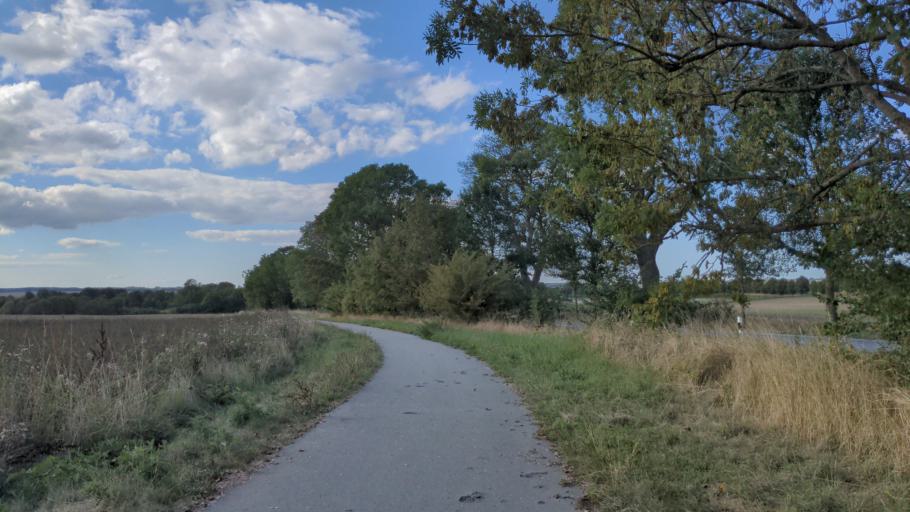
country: DE
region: Mecklenburg-Vorpommern
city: Klutz
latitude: 53.9621
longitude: 11.1823
